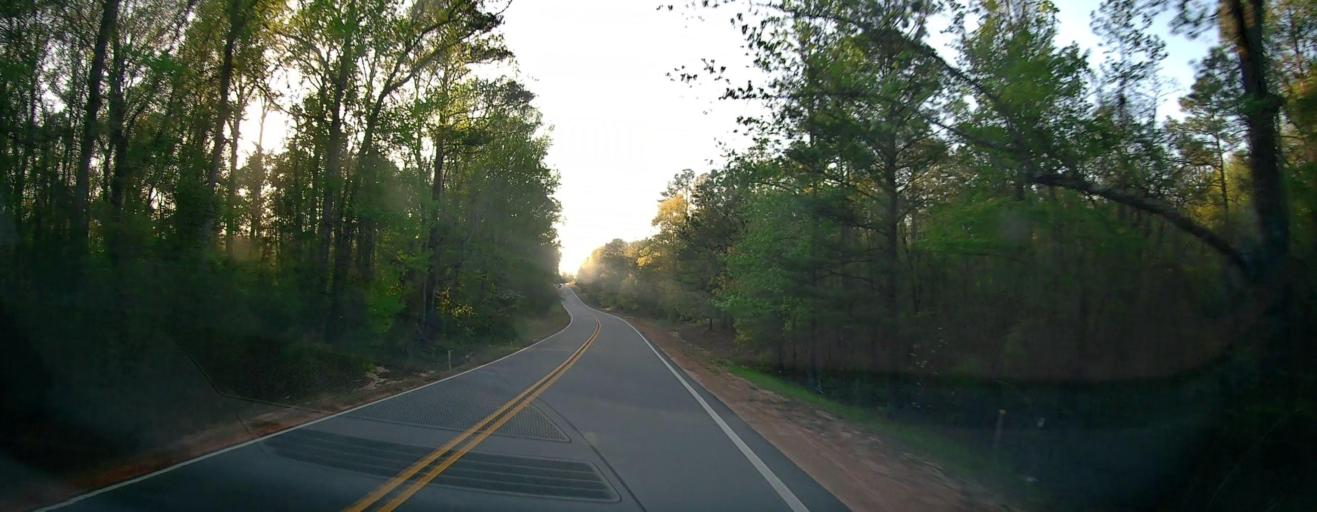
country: US
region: Georgia
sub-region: Talbot County
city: Talbotton
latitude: 32.5307
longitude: -84.4830
